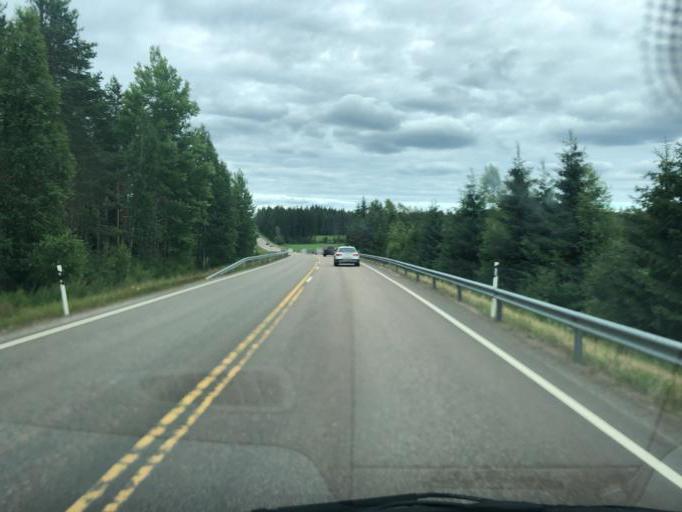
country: FI
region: Southern Savonia
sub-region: Mikkeli
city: Maentyharju
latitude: 61.0610
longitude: 27.0495
